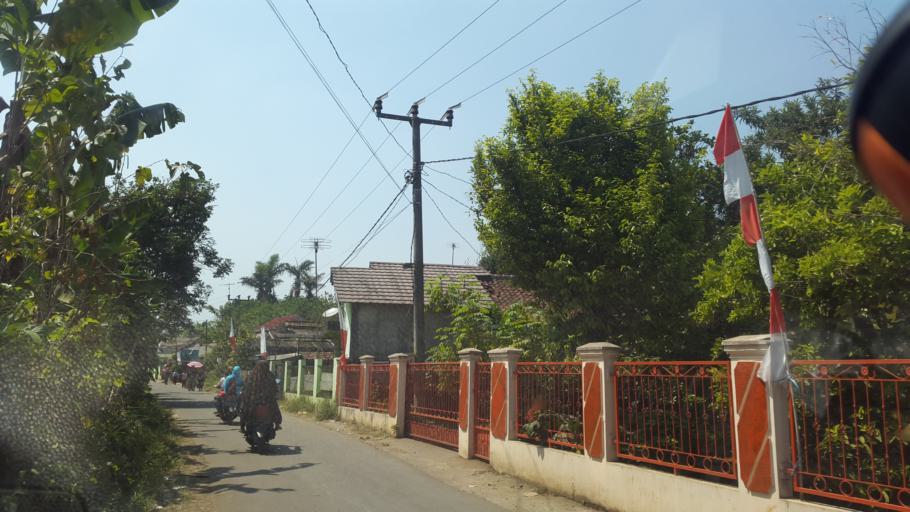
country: ID
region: West Java
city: Cicurug
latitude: -6.8605
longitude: 106.7993
